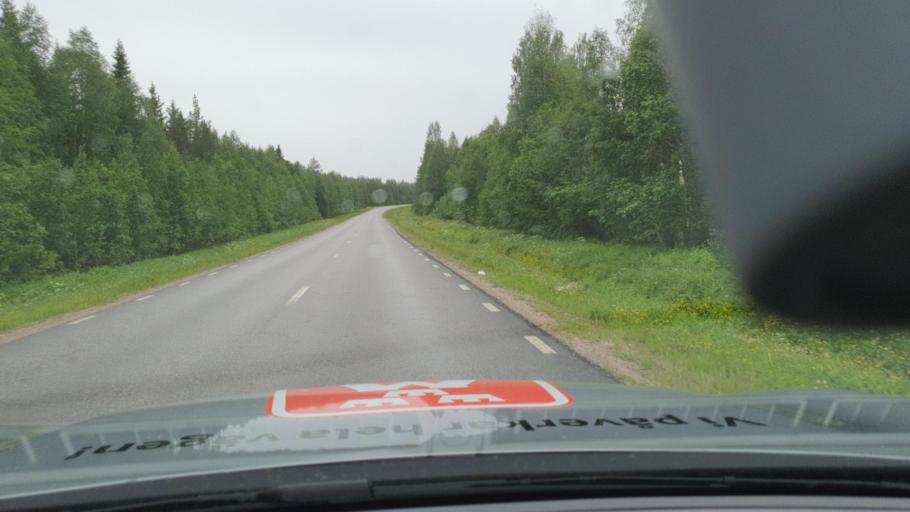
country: SE
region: Norrbotten
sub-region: Overtornea Kommun
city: OEvertornea
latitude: 66.4145
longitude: 23.4285
